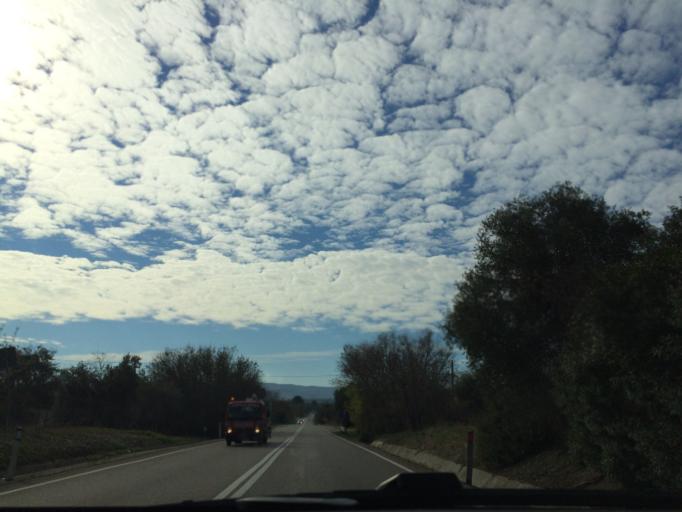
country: IT
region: Basilicate
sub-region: Provincia di Matera
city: Matera
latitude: 40.6148
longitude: 16.5774
